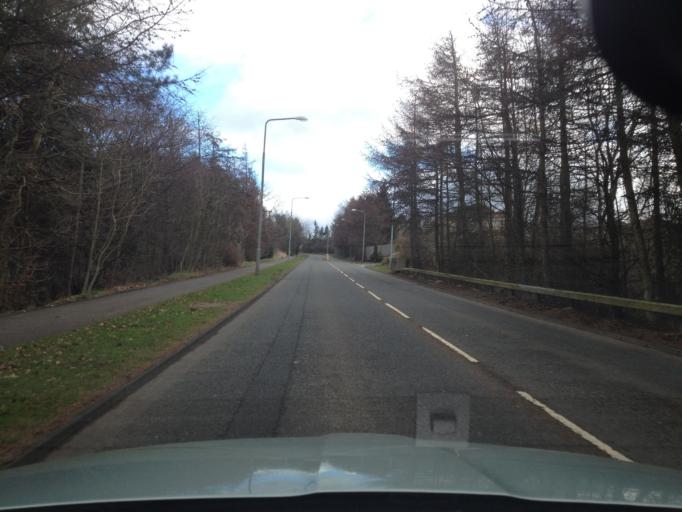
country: GB
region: Scotland
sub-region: West Lothian
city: Livingston
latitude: 55.8590
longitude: -3.5175
